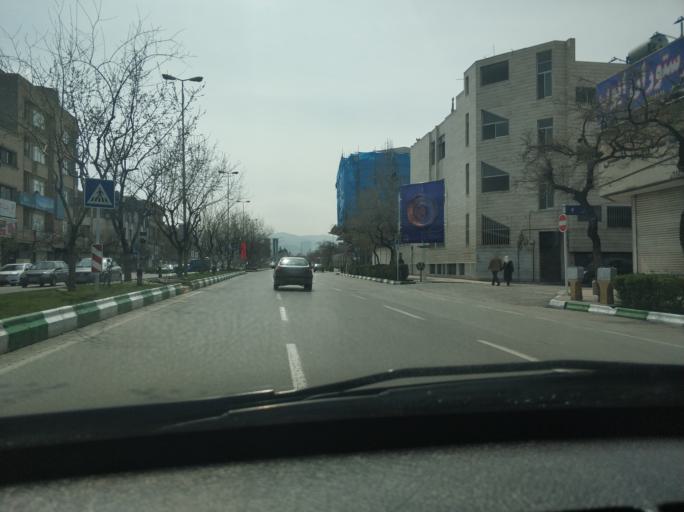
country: IR
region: Razavi Khorasan
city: Mashhad
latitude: 36.3024
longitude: 59.5644
